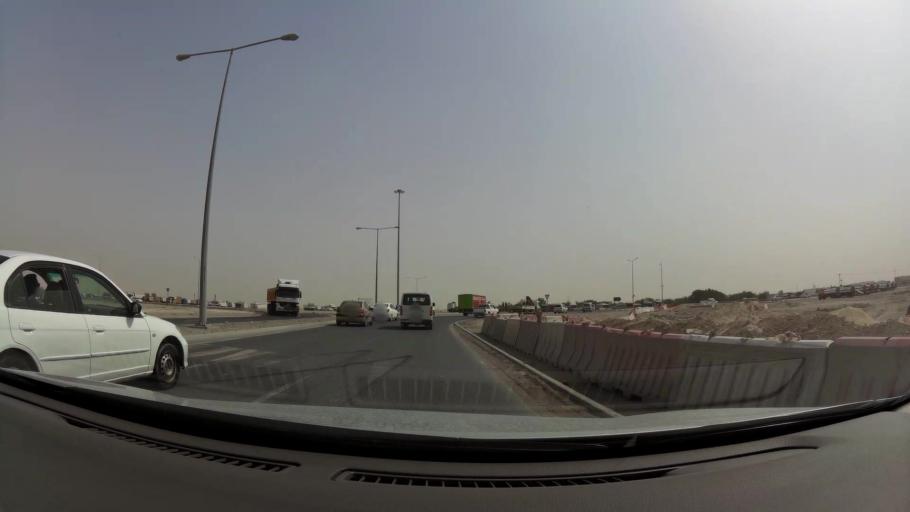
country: QA
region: Baladiyat ar Rayyan
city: Ar Rayyan
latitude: 25.2297
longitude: 51.3851
